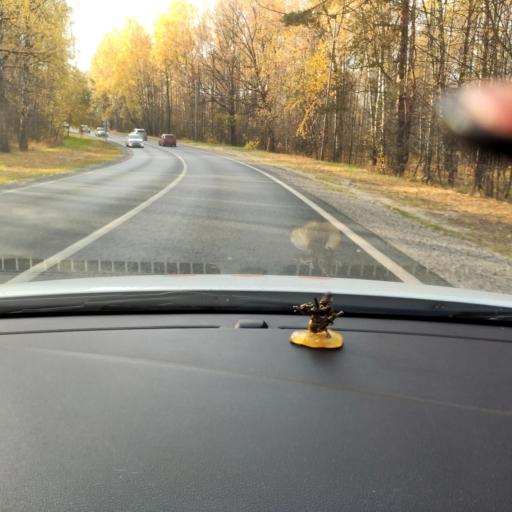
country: RU
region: Tatarstan
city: Osinovo
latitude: 55.8365
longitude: 48.8931
